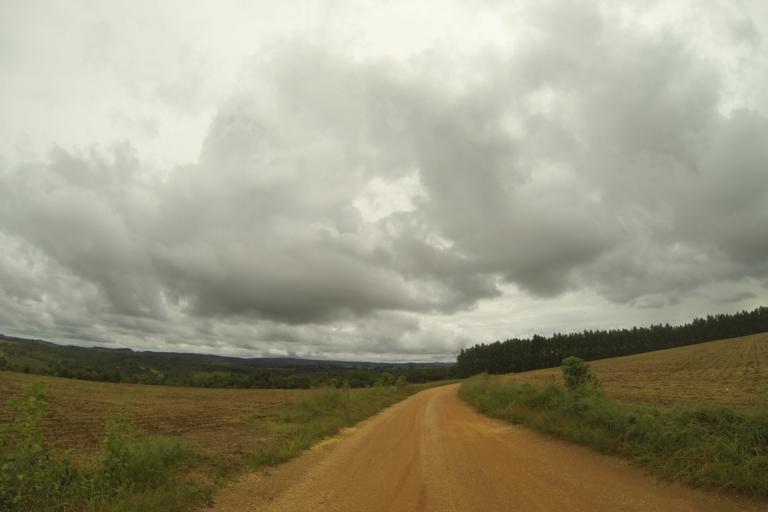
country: BR
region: Minas Gerais
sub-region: Ibia
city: Ibia
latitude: -19.7213
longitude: -46.5827
